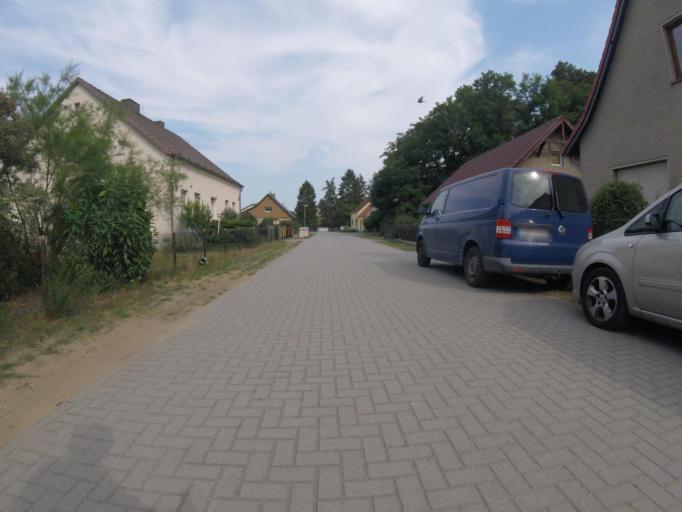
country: DE
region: Brandenburg
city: Erkner
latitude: 52.3147
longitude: 13.7448
